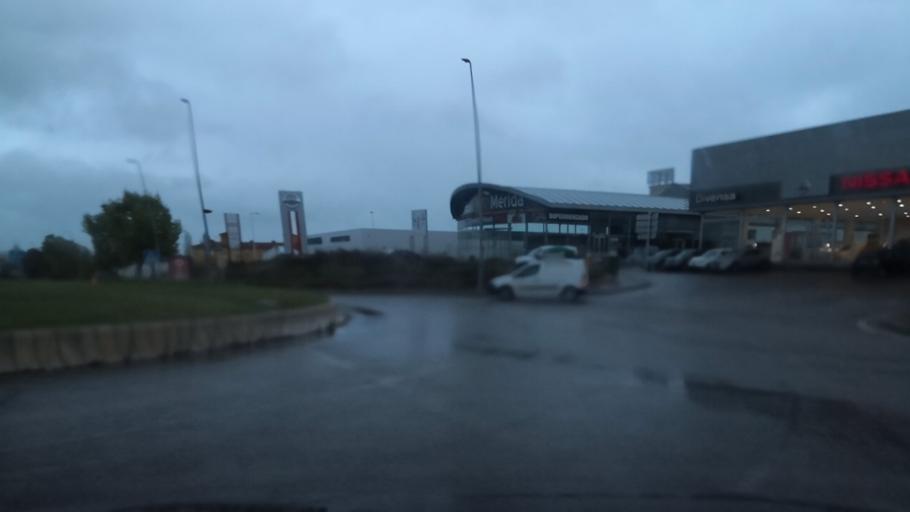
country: ES
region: Extremadura
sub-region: Provincia de Badajoz
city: Merida
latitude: 38.9048
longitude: -6.3644
